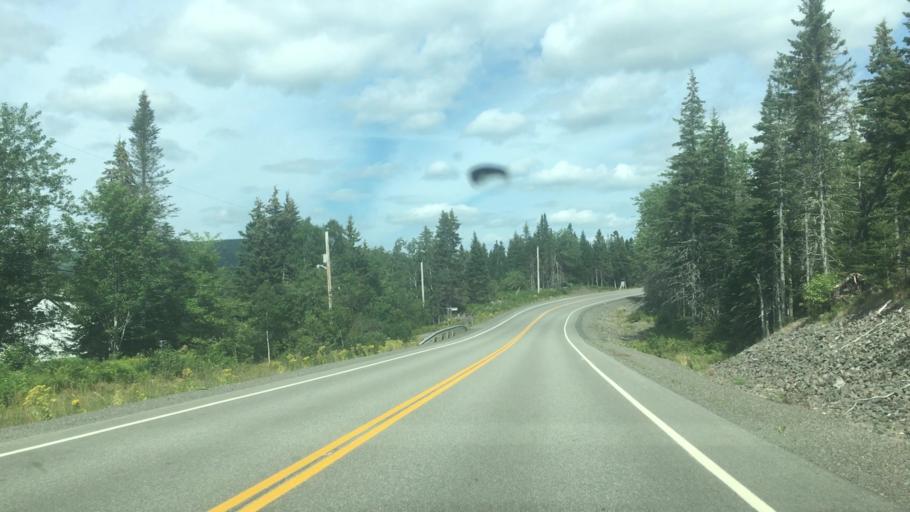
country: CA
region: Nova Scotia
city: Sydney Mines
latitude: 46.3252
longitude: -60.6065
